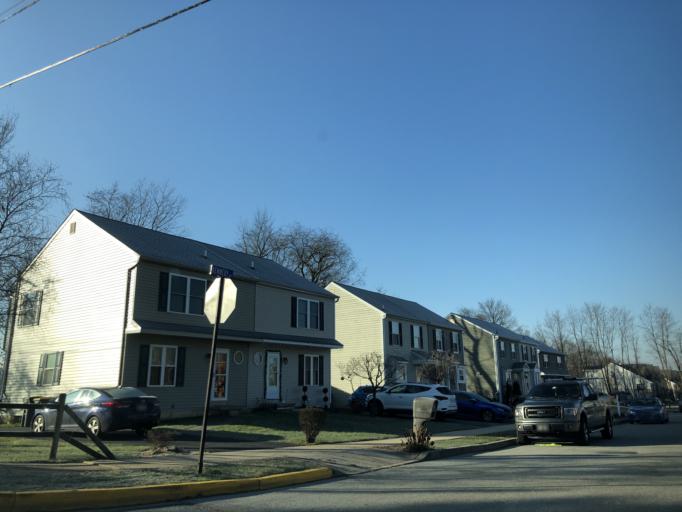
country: US
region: Pennsylvania
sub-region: Chester County
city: Downingtown
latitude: 40.0040
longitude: -75.6943
